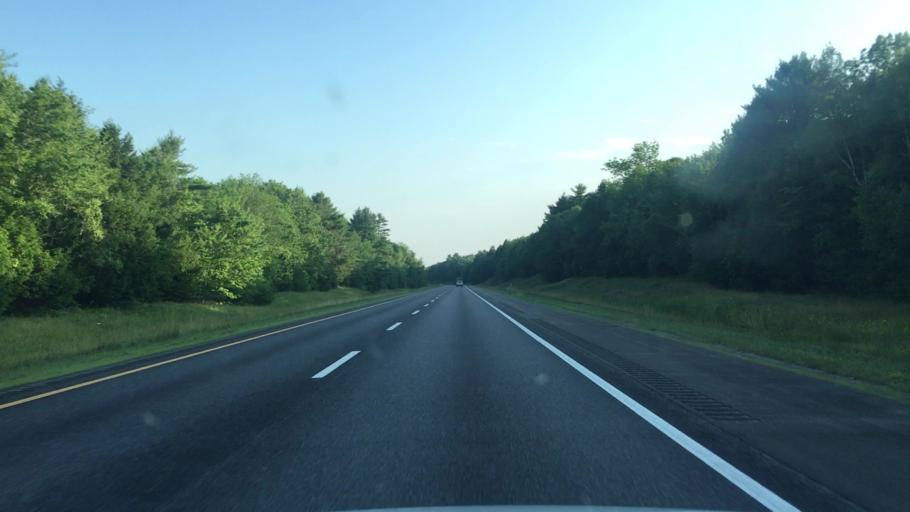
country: US
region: Maine
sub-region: Sagadahoc County
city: Richmond
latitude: 44.0577
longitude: -69.8886
